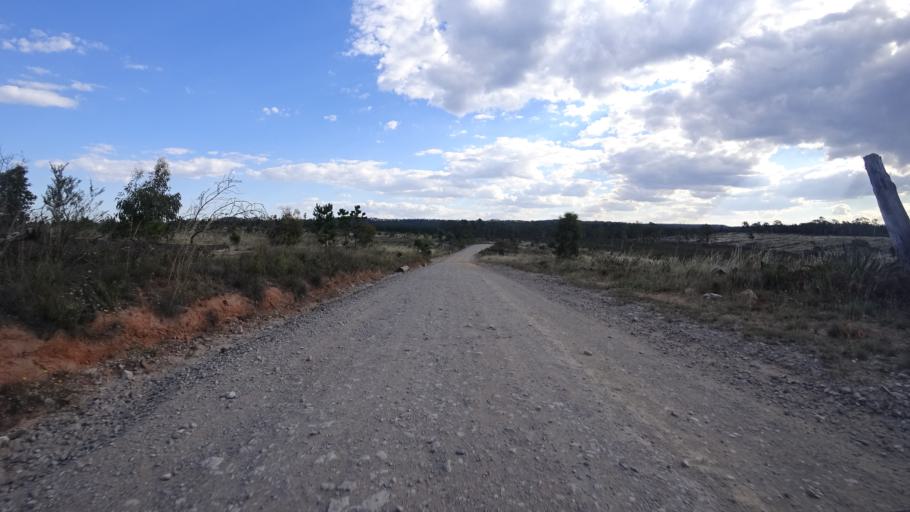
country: AU
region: New South Wales
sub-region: Lithgow
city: Lithgow
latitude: -33.3799
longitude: 150.2419
